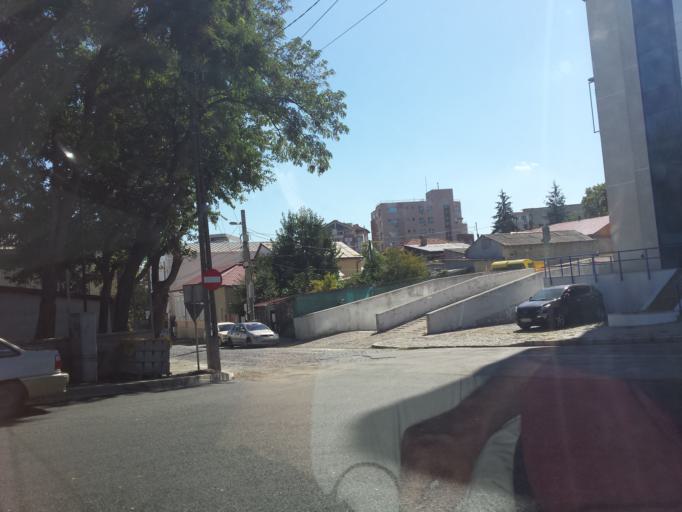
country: RO
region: Tulcea
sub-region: Municipiul Tulcea
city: Tulcea
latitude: 45.1723
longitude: 28.7960
